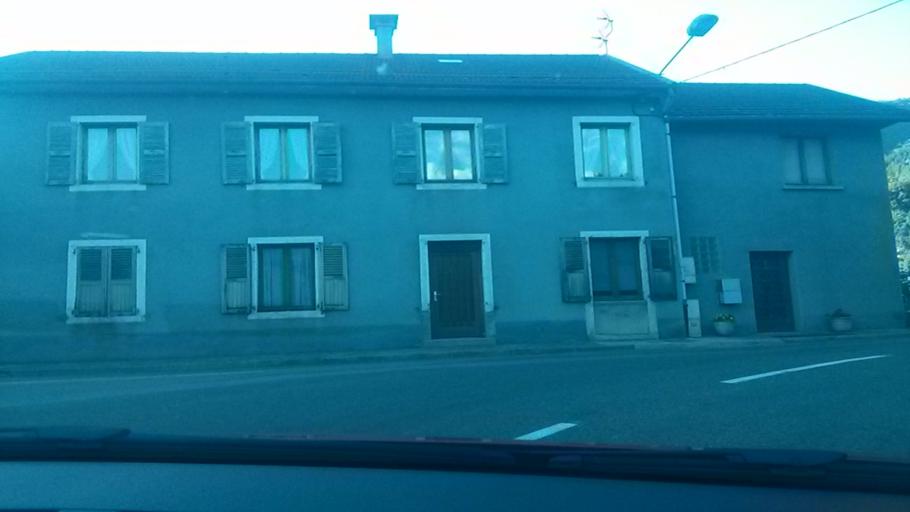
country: FR
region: Franche-Comte
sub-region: Departement du Jura
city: Saint-Claude
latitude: 46.3769
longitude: 5.8726
